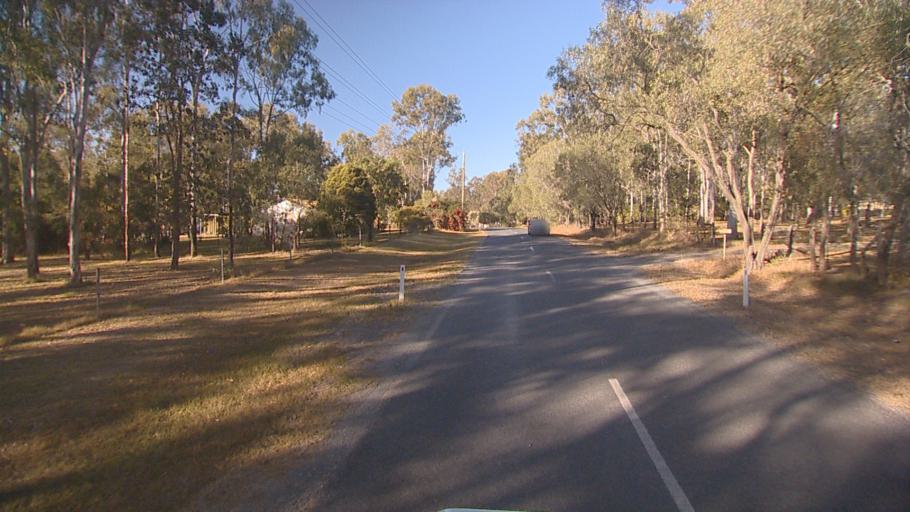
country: AU
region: Queensland
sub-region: Logan
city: North Maclean
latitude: -27.7929
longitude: 152.9877
